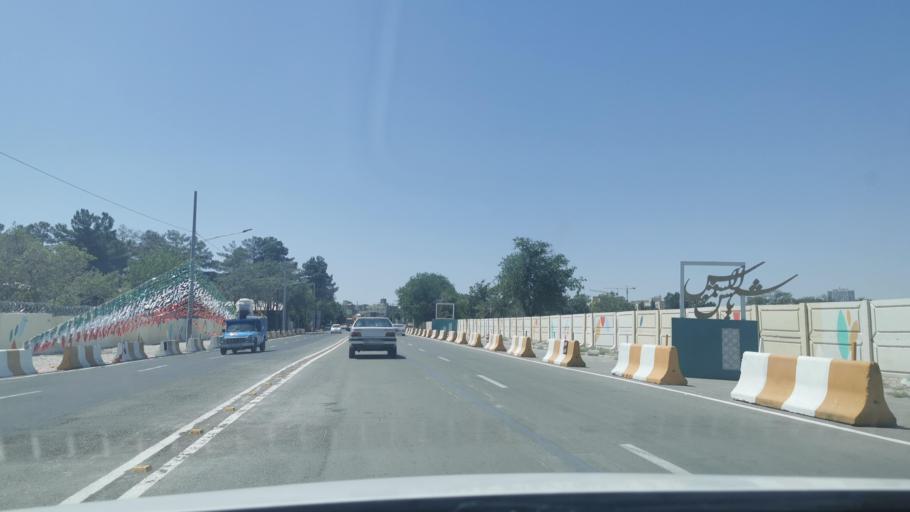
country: IR
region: Razavi Khorasan
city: Mashhad
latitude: 36.2743
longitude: 59.5811
